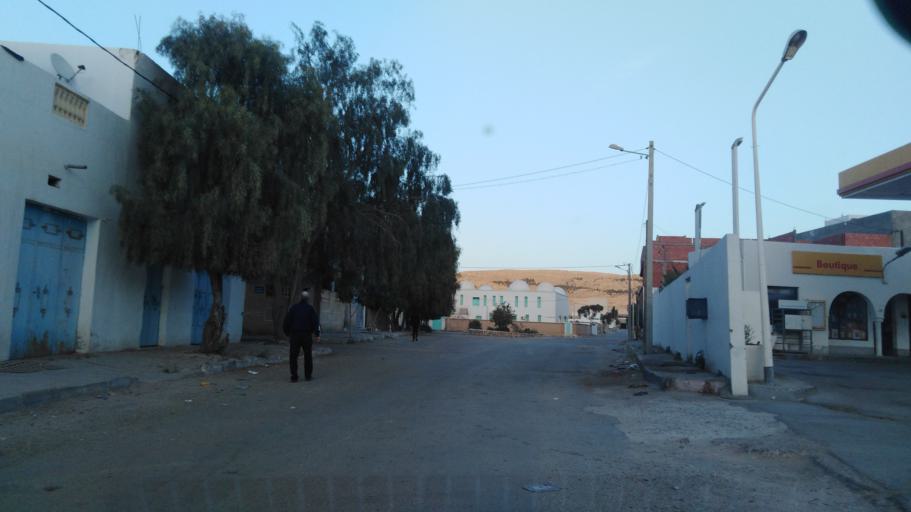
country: TN
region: Tataouine
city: Tataouine
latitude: 32.9410
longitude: 10.4526
